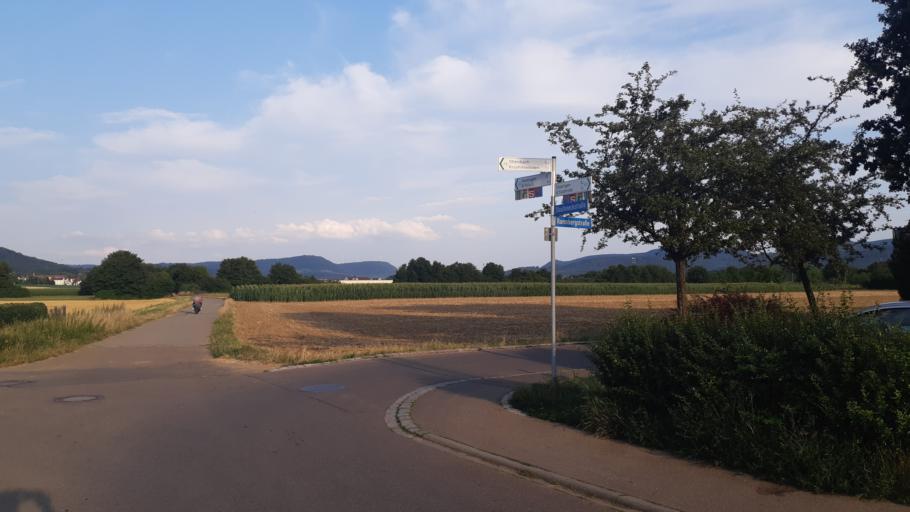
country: DE
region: Baden-Wuerttemberg
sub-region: Regierungsbezirk Stuttgart
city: Eislingen
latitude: 48.6988
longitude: 9.7217
